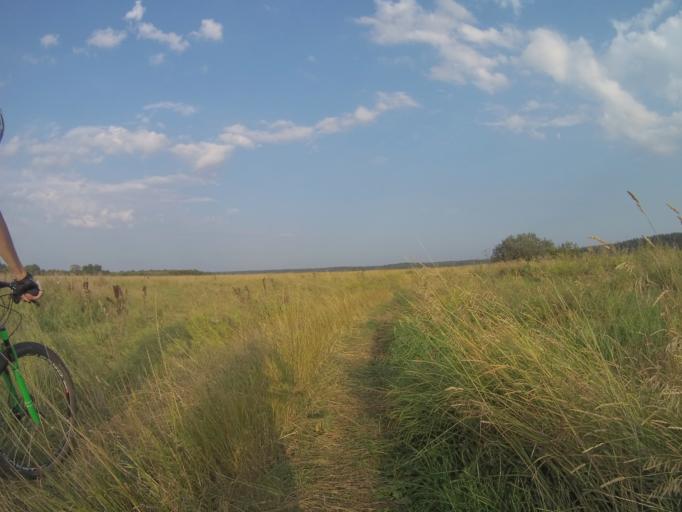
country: RU
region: Vladimir
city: Orgtrud
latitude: 56.3056
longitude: 40.6534
